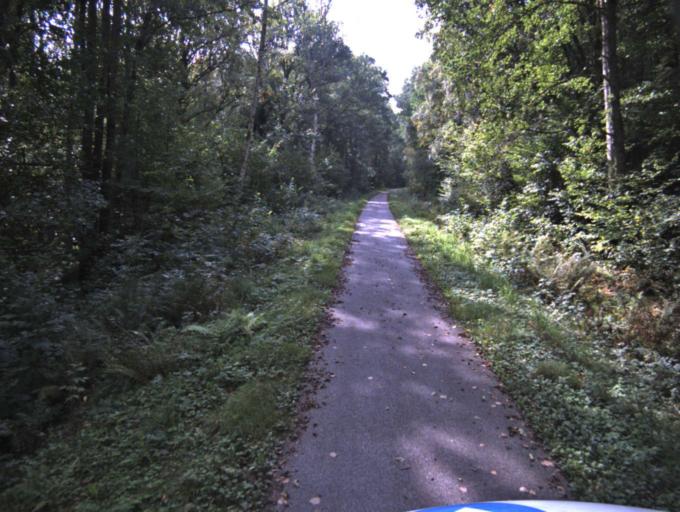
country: SE
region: Vaestra Goetaland
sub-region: Tranemo Kommun
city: Limmared
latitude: 57.6450
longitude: 13.3597
